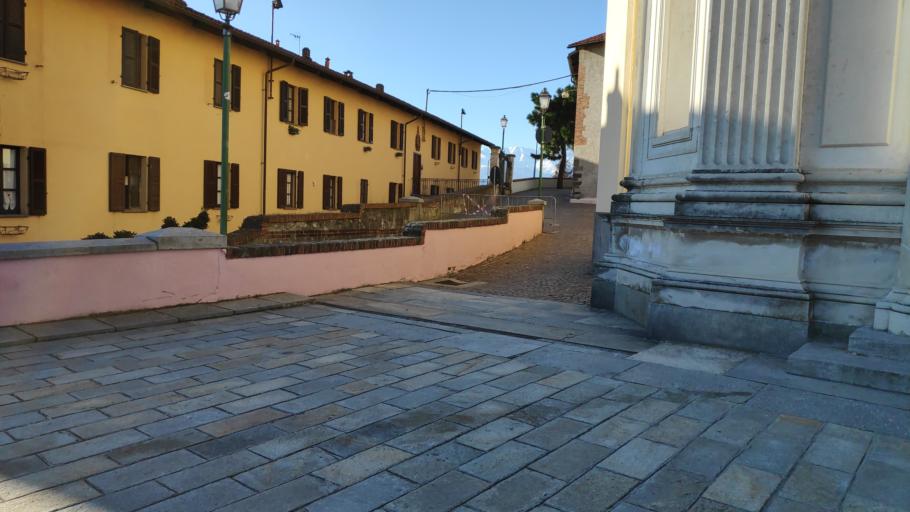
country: IT
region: Piedmont
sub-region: Provincia di Torino
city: Pinerolo
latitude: 44.8895
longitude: 7.3276
